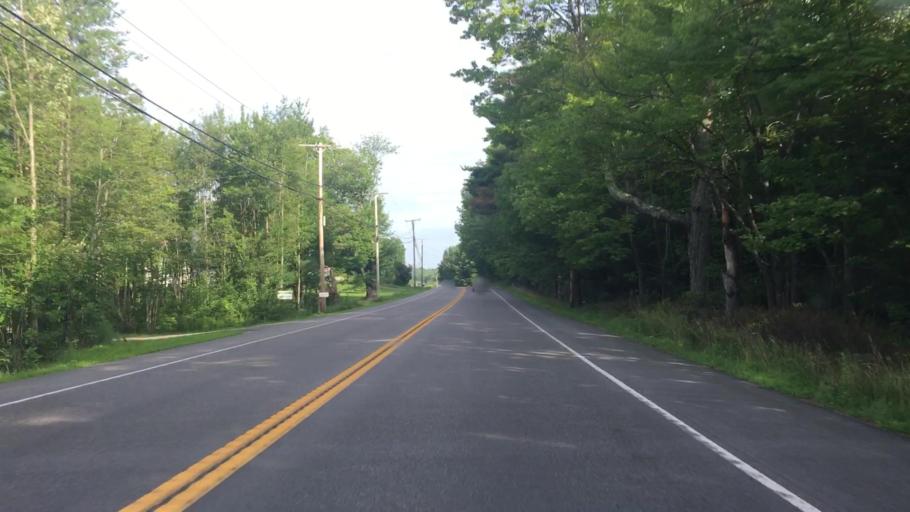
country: US
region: Maine
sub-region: Cumberland County
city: Gorham
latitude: 43.7040
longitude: -70.5036
